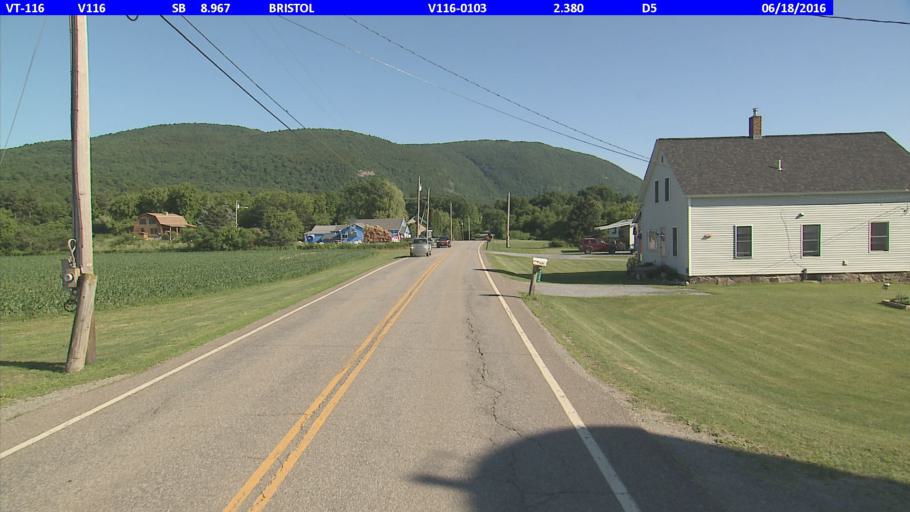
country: US
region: Vermont
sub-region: Addison County
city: Bristol
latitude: 44.0876
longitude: -73.0903
